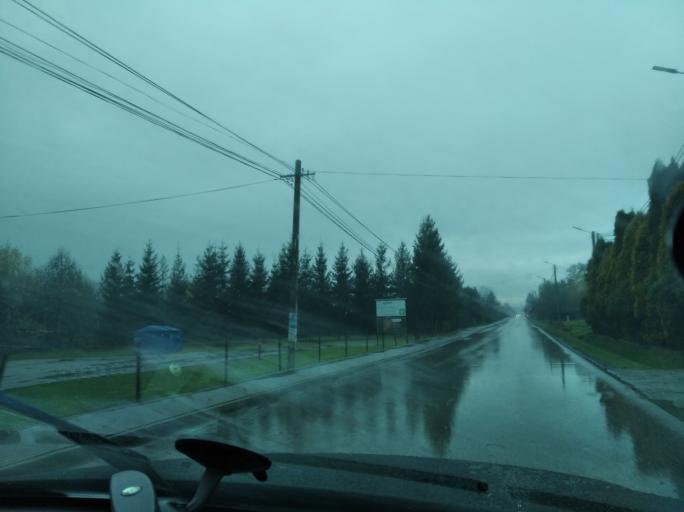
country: PL
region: Subcarpathian Voivodeship
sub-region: Powiat lancucki
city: Kraczkowa
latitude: 50.0382
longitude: 22.1659
